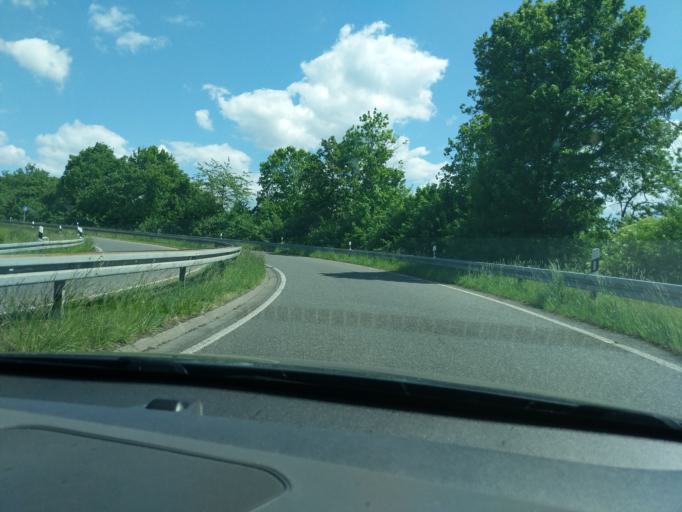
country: DE
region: Hesse
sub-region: Regierungsbezirk Darmstadt
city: Maintal
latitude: 50.1471
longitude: 8.8268
